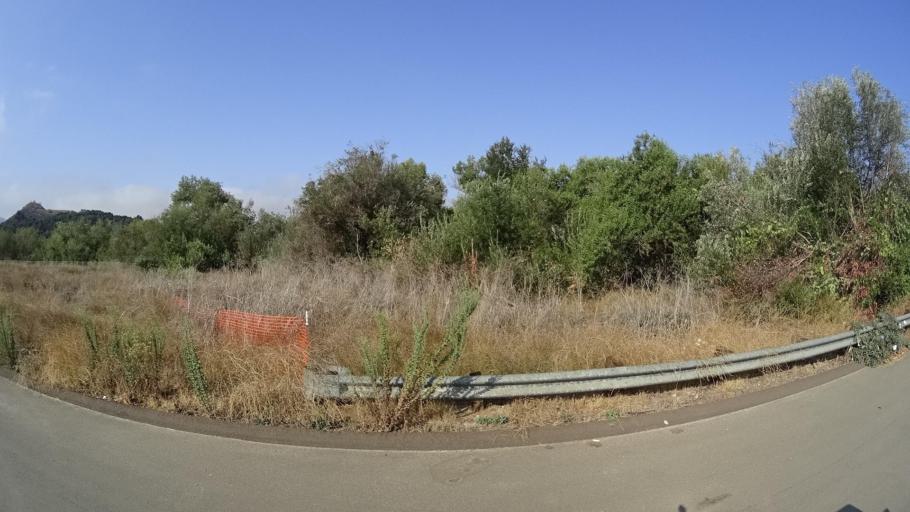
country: US
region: California
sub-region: San Diego County
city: Rainbow
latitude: 33.3374
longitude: -117.1522
